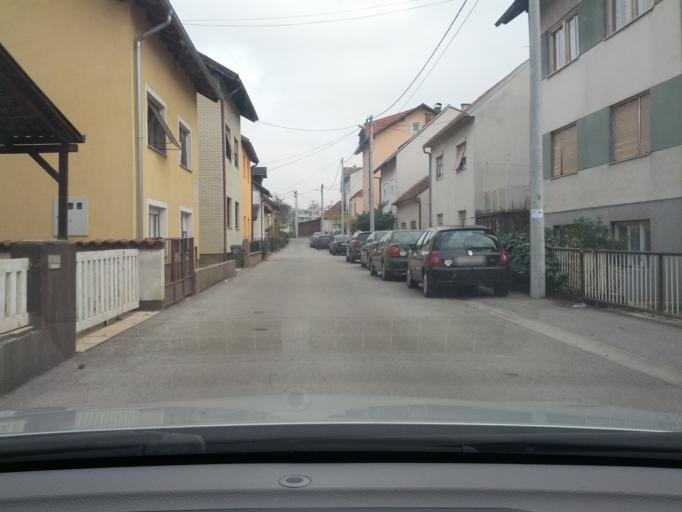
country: HR
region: Grad Zagreb
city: Jankomir
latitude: 45.8093
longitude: 15.9231
